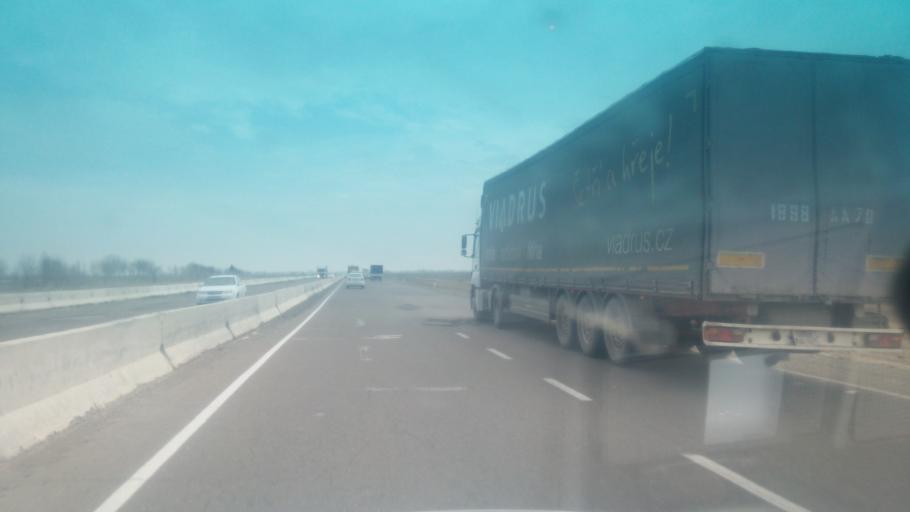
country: KZ
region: Ongtustik Qazaqstan
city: Myrzakent
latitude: 40.5146
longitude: 68.4857
